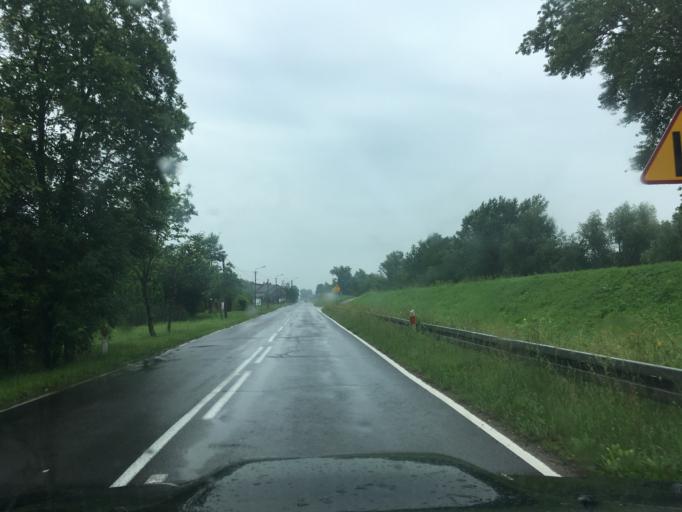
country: PL
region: Masovian Voivodeship
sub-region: Powiat piaseczynski
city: Gora Kalwaria
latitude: 51.9904
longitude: 21.2419
